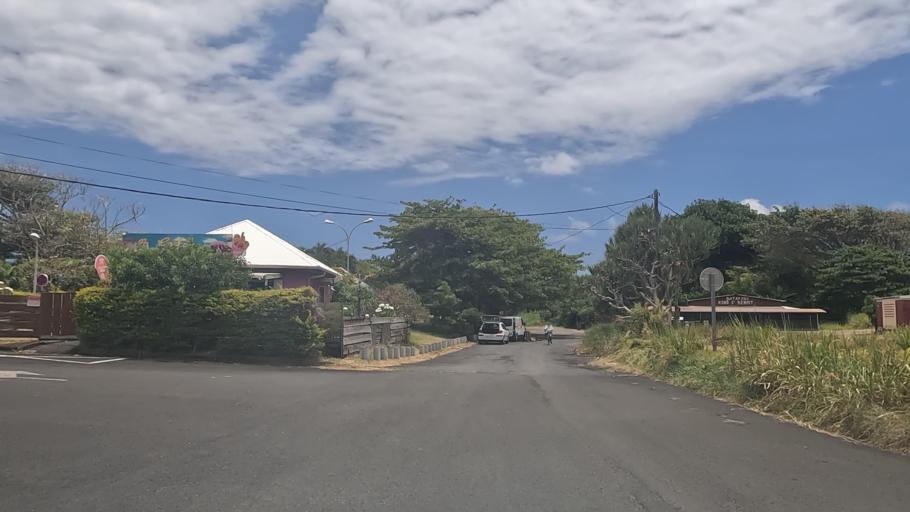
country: RE
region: Reunion
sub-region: Reunion
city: Saint-Benoit
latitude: -21.0346
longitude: 55.7169
